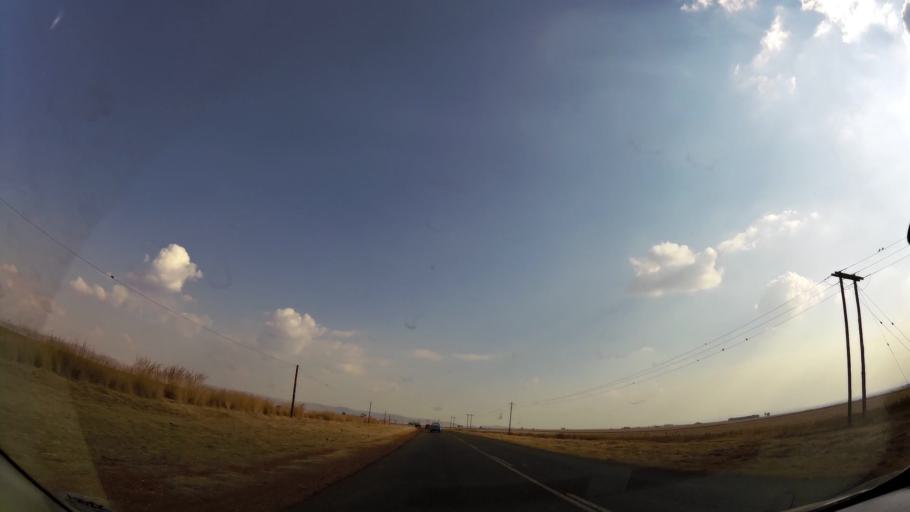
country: ZA
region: Gauteng
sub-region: Sedibeng District Municipality
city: Heidelberg
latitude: -26.3909
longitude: 28.2939
